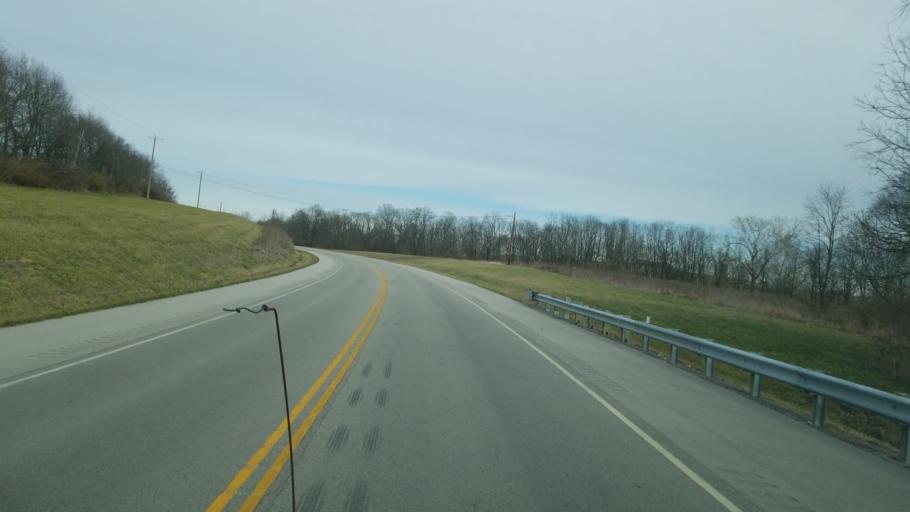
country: US
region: Ohio
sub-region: Brown County
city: Aberdeen
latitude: 38.5949
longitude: -83.8148
